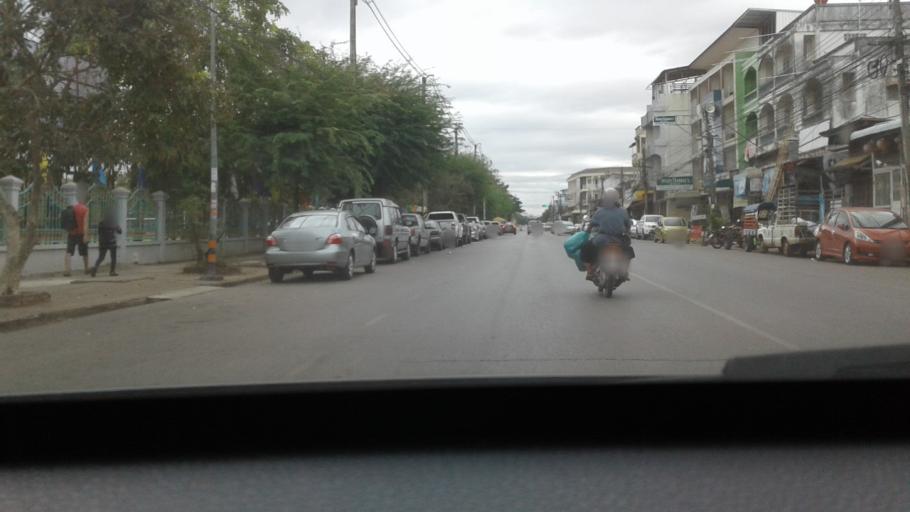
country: TH
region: Changwat Udon Thani
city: Udon Thani
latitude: 17.4023
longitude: 102.7901
